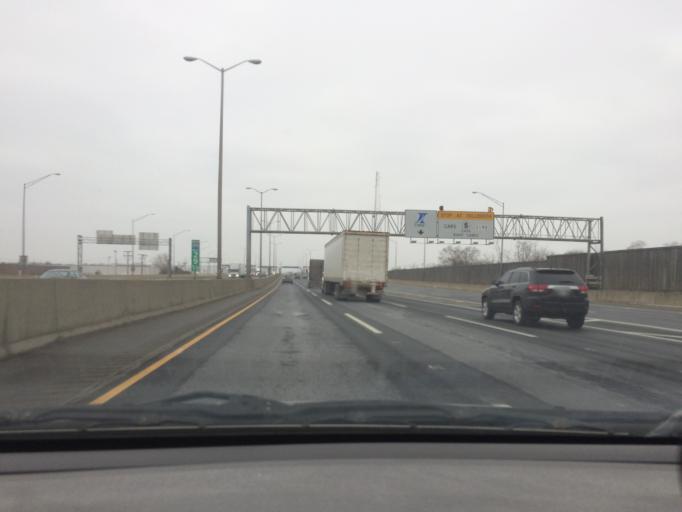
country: US
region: Illinois
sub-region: DuPage County
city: Glendale Heights
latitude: 41.9276
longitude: -88.0379
